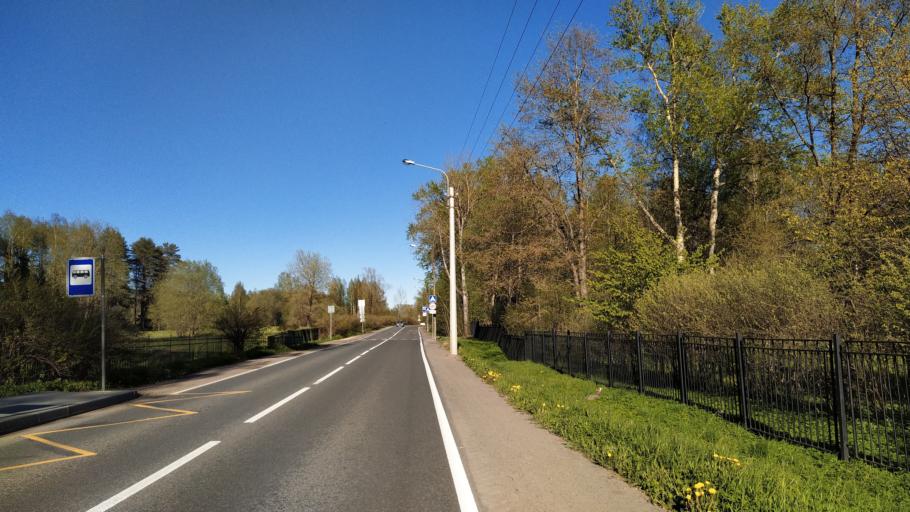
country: RU
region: St.-Petersburg
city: Tyarlevo
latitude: 59.6853
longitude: 30.4764
